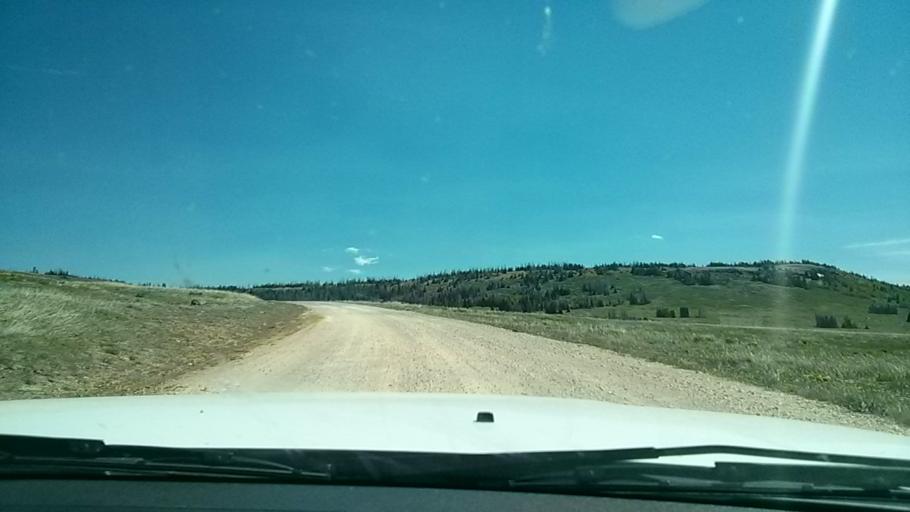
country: US
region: Utah
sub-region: Iron County
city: Parowan
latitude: 37.6735
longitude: -112.8275
